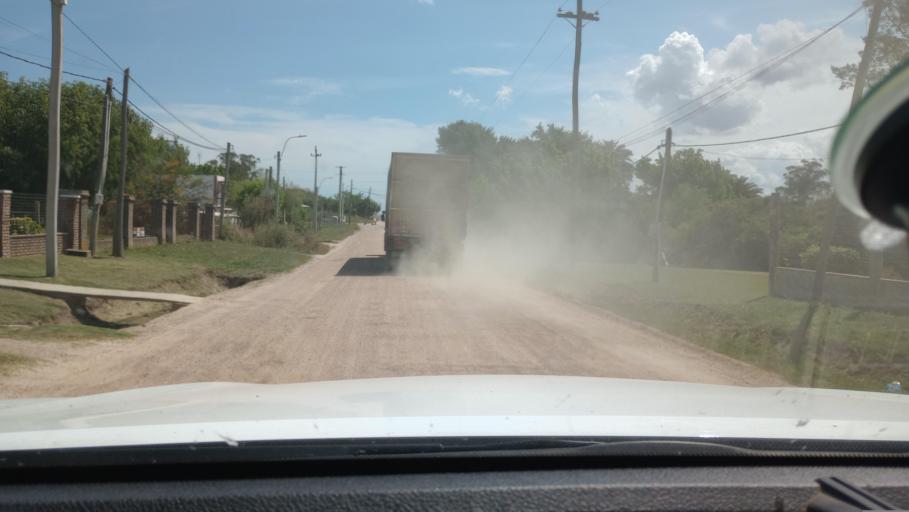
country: UY
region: Canelones
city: Sauce
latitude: -34.6600
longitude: -56.0587
